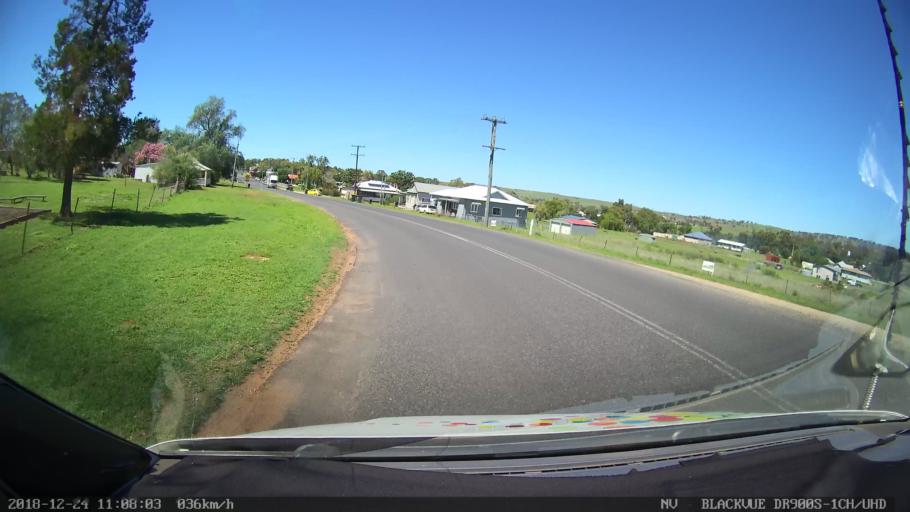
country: AU
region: New South Wales
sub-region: Upper Hunter Shire
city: Merriwa
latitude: -32.1354
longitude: 150.3566
